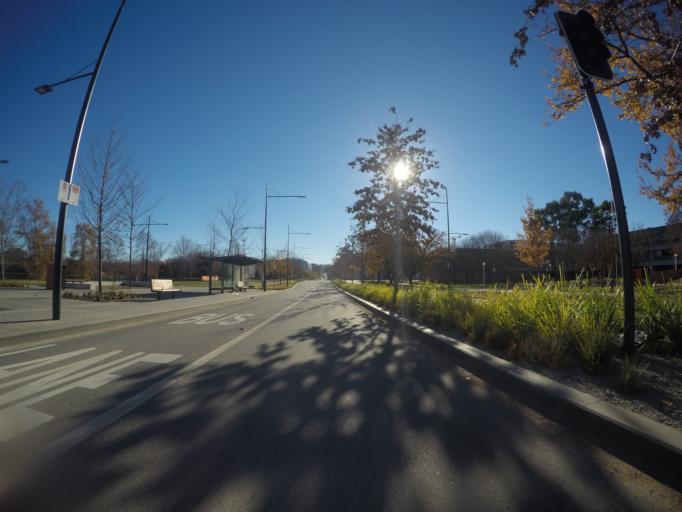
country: AU
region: Australian Capital Territory
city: Canberra
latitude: -35.2864
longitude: 149.1362
